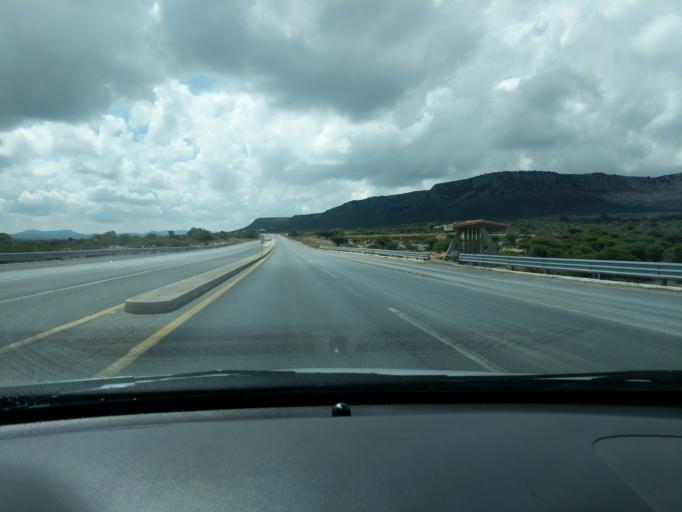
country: MX
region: Zacatecas
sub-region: Pinos
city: Santiago
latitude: 22.4050
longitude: -101.3879
